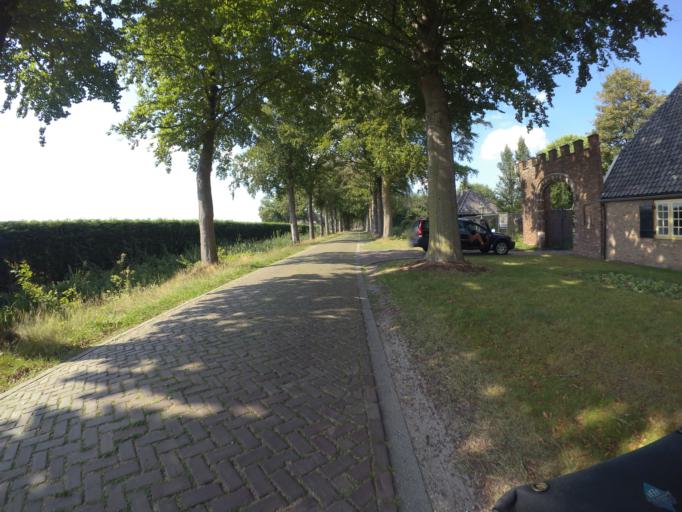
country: NL
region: North Brabant
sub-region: Gemeente Schijndel
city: Schijndel
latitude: 51.6594
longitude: 5.4136
